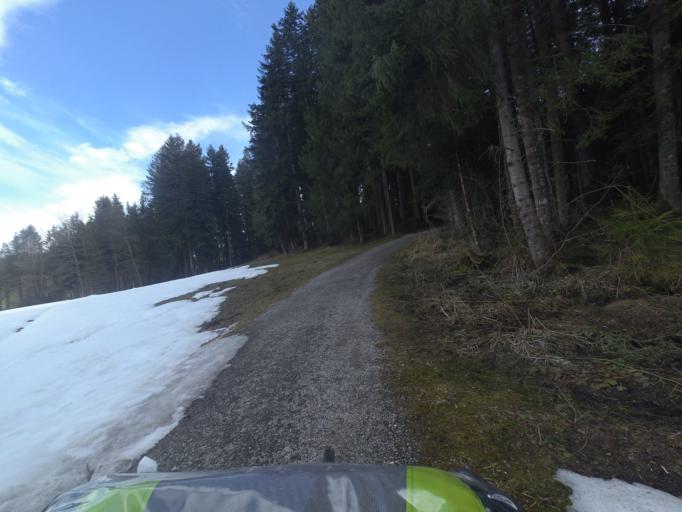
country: AT
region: Salzburg
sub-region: Politischer Bezirk Hallein
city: Abtenau
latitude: 47.5765
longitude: 13.3451
